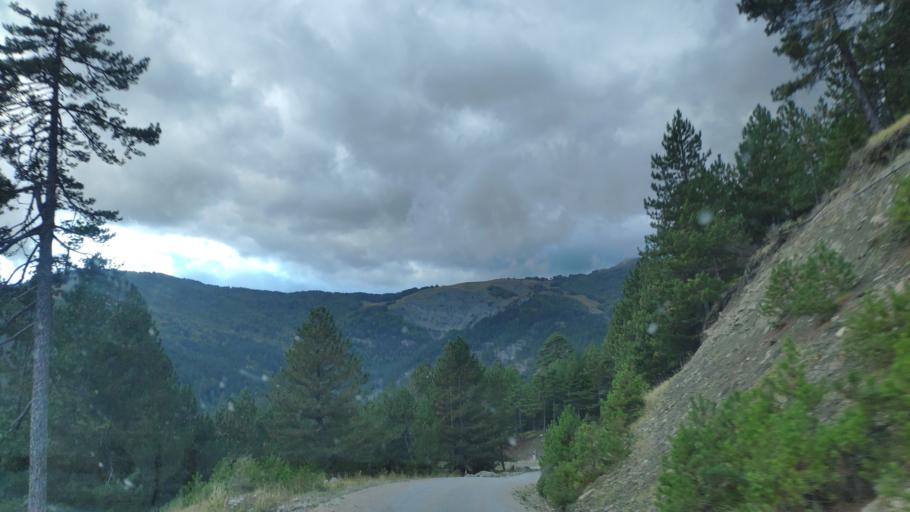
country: AL
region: Korce
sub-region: Rrethi i Kolonjes
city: Erseke
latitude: 40.2906
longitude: 20.8589
